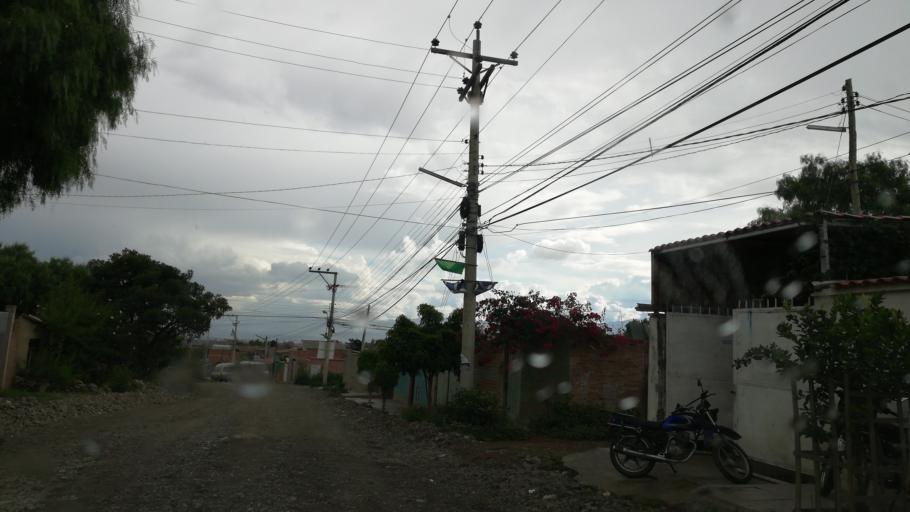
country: BO
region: Cochabamba
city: Cochabamba
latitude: -17.3414
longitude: -66.2000
